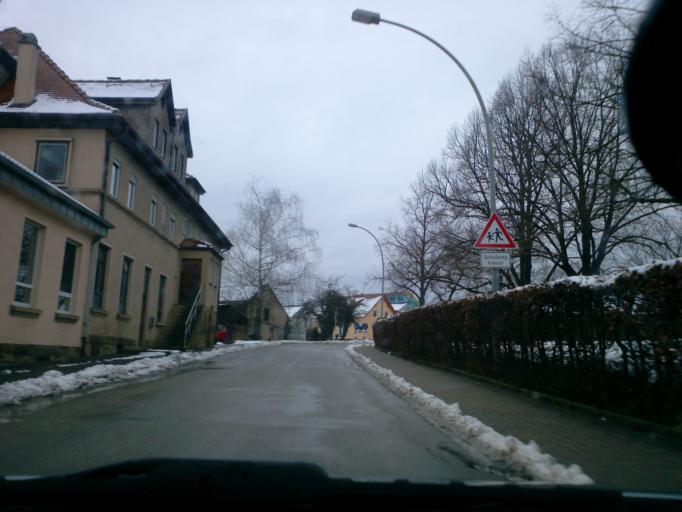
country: DE
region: Baden-Wuerttemberg
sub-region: Regierungsbezirk Stuttgart
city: Brackenheim
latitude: 49.0683
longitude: 9.0874
